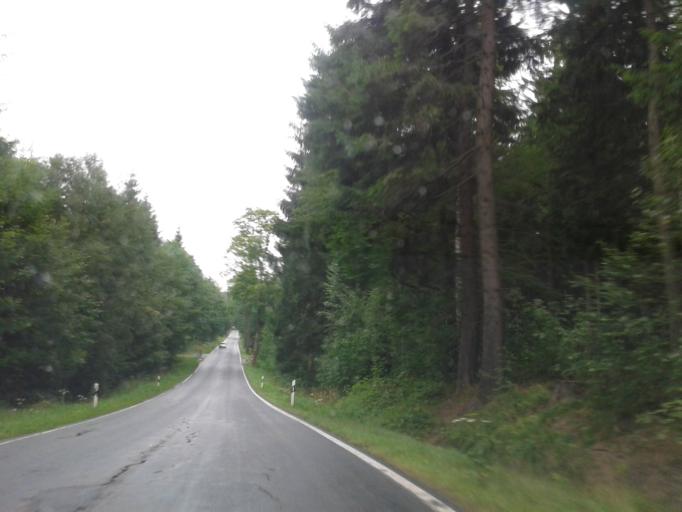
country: DE
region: Saxony
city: Dorfhain
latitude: 50.9600
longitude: 13.5183
